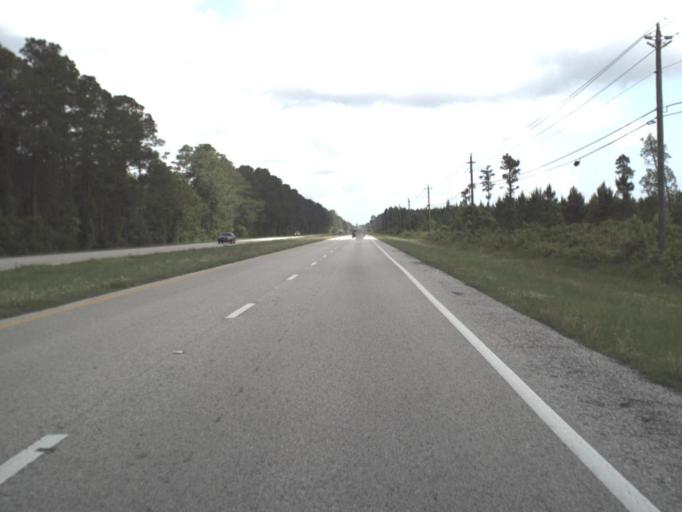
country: US
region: Florida
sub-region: Saint Johns County
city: Butler Beach
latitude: 29.7000
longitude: -81.2976
